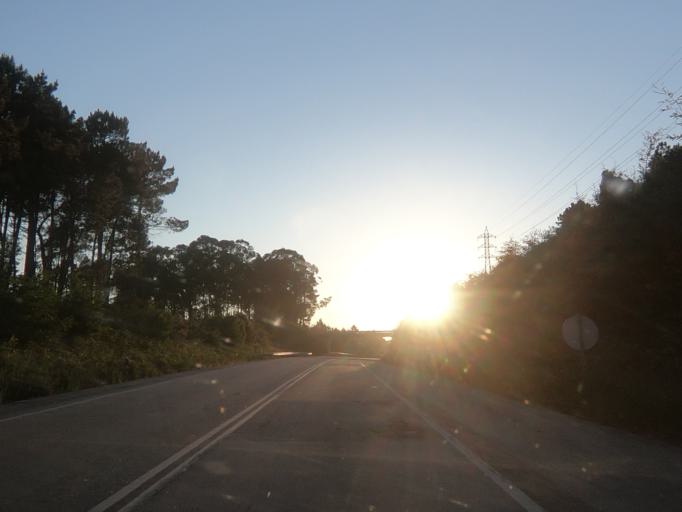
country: PT
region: Viseu
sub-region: Viseu
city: Rio de Loba
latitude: 40.6757
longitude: -7.8683
